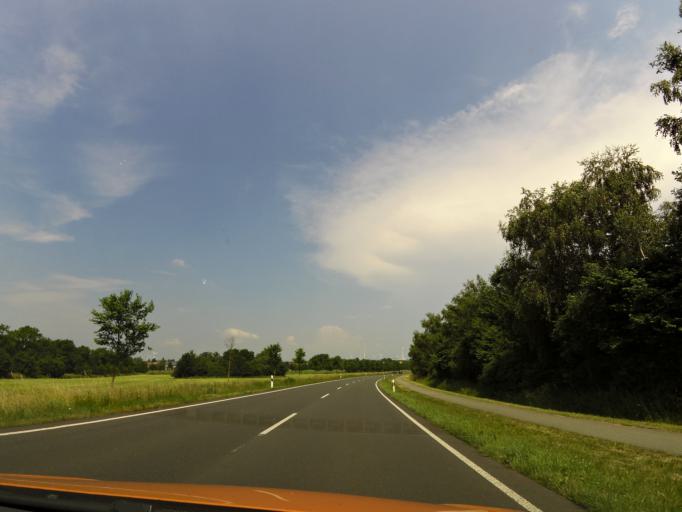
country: DE
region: Brandenburg
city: Gerdshagen
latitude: 53.2009
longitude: 12.2043
